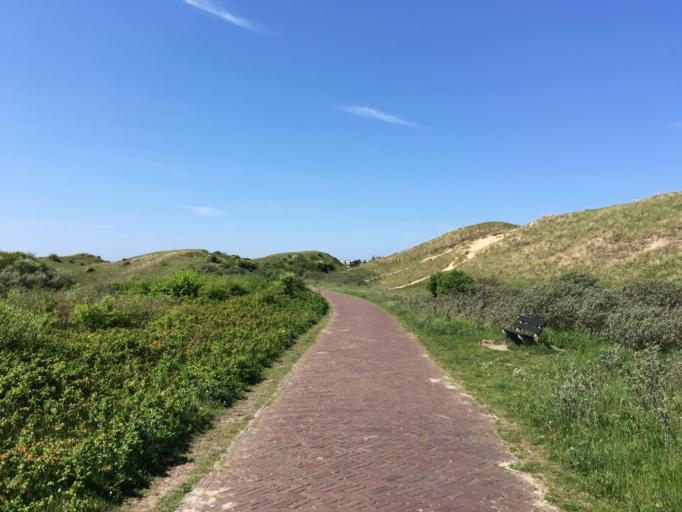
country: NL
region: North Holland
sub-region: Gemeente Bergen
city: Egmond aan Zee
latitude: 52.6162
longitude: 4.6344
